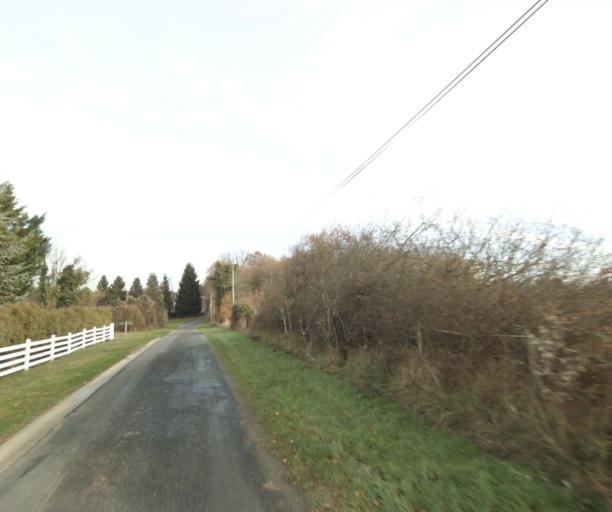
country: FR
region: Poitou-Charentes
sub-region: Departement de la Charente-Maritime
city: Saint-Hilaire-de-Villefranche
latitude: 45.8164
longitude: -0.5608
